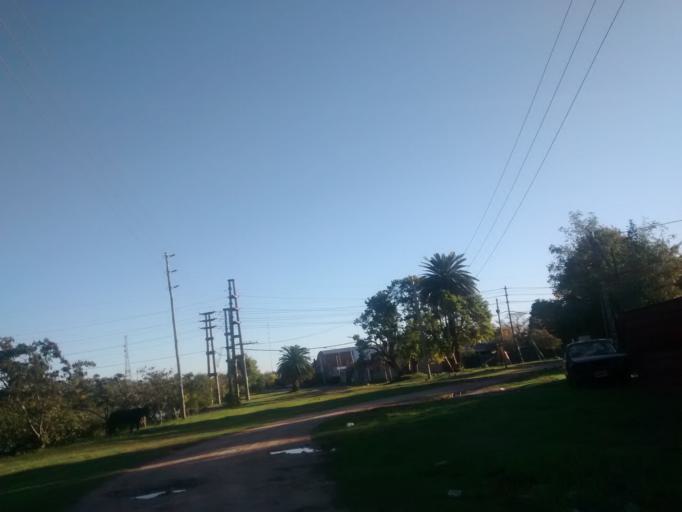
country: AR
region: Buenos Aires
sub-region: Partido de La Plata
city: La Plata
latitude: -34.8948
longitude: -57.9295
